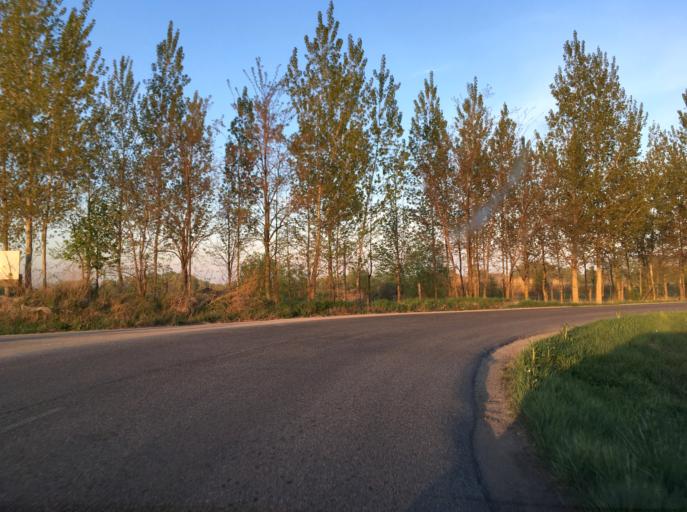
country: SK
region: Trnavsky
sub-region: Okres Dunajska Streda
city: Velky Meder
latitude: 47.9078
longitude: 17.8619
